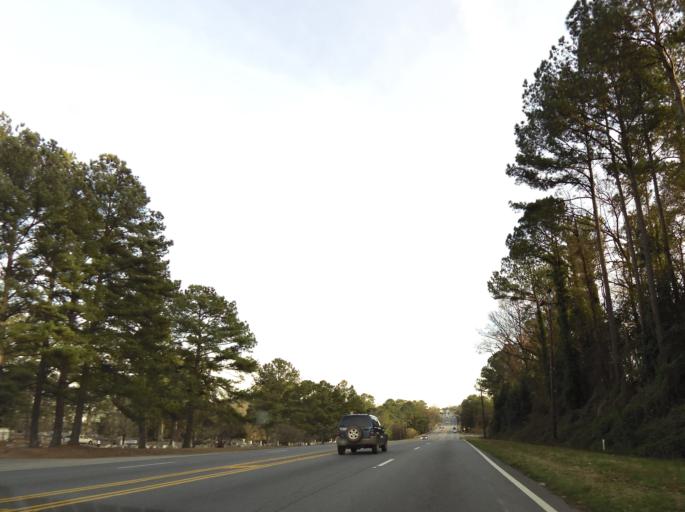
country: US
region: Georgia
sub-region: Bibb County
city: Macon
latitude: 32.8546
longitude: -83.6440
